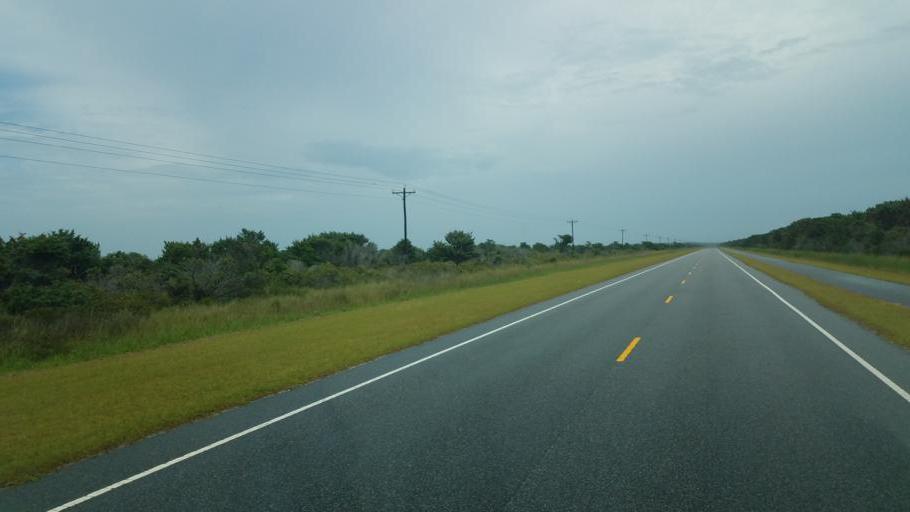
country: US
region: North Carolina
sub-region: Dare County
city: Buxton
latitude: 35.1122
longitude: -75.9481
